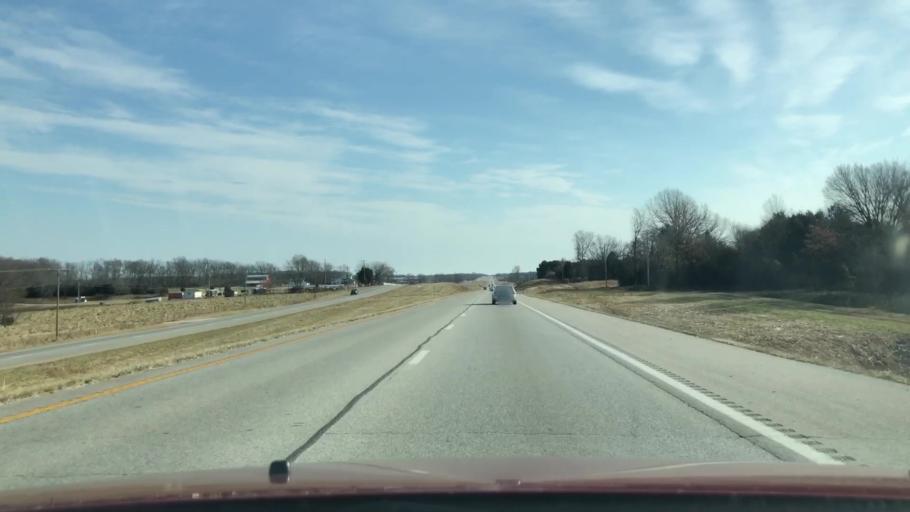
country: US
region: Missouri
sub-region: Christian County
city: Ozark
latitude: 37.1195
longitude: -93.1637
